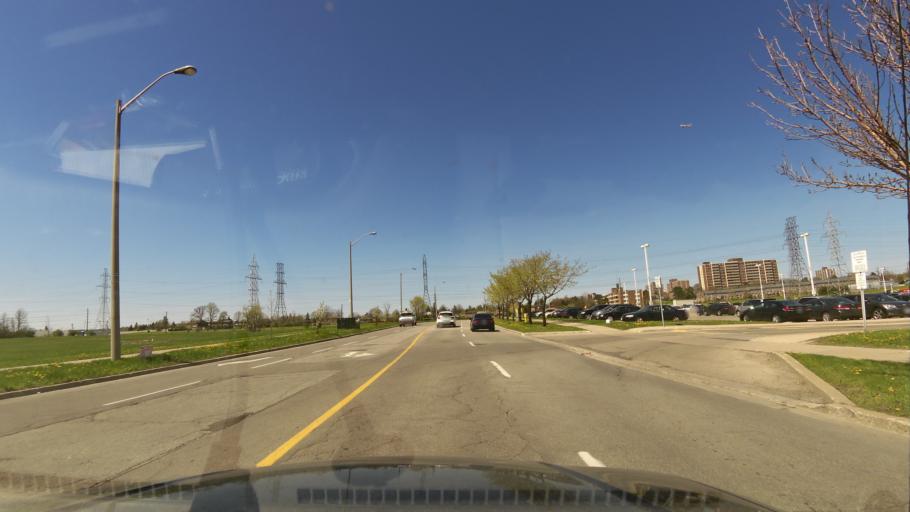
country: CA
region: Ontario
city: Concord
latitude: 43.7575
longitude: -79.5210
